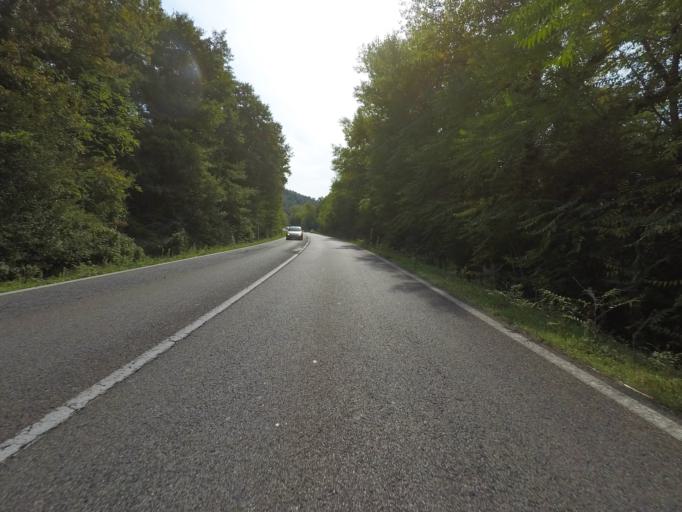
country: IT
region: Tuscany
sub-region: Provincia di Siena
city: Rosia
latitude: 43.1947
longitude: 11.2768
